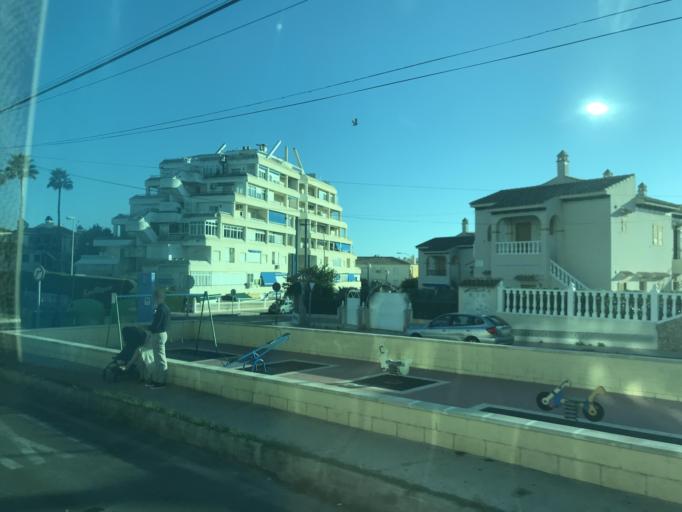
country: ES
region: Valencia
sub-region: Provincia de Alicante
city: Torrevieja
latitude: 38.0038
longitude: -0.6552
